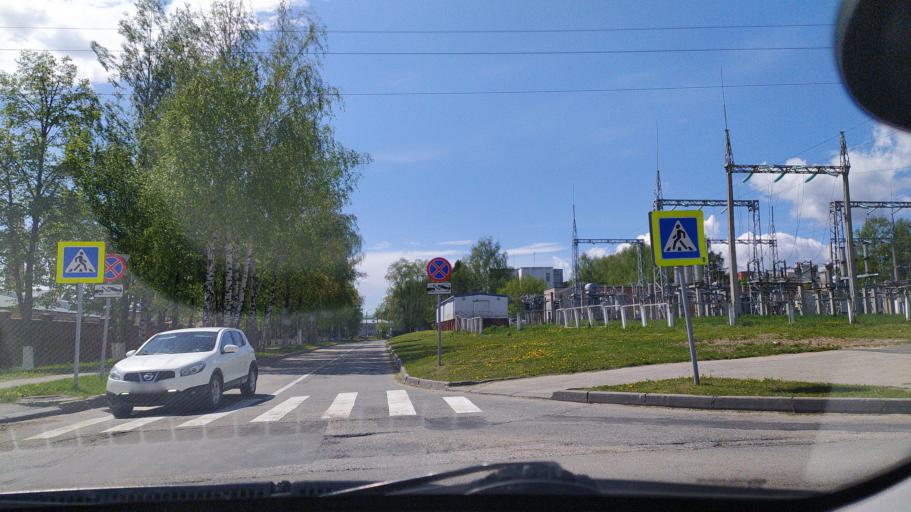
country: RU
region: Chuvashia
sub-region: Cheboksarskiy Rayon
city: Cheboksary
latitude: 56.1408
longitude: 47.2084
